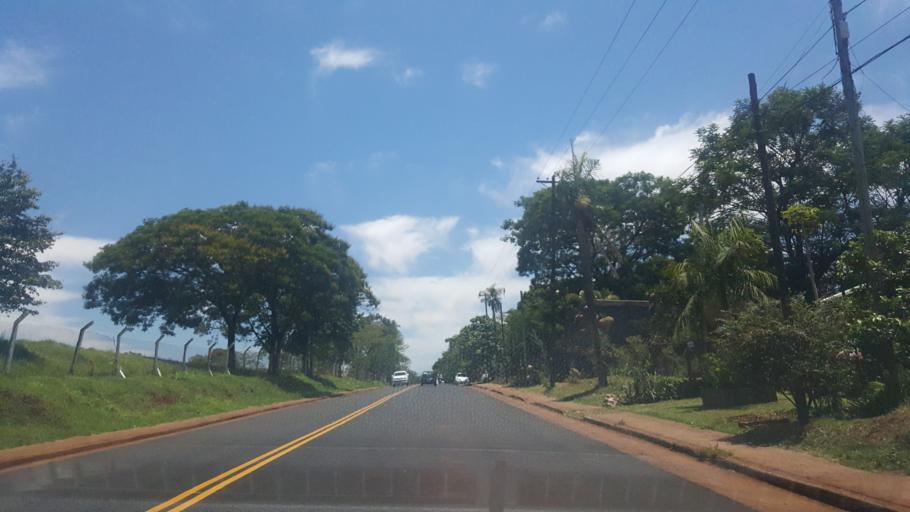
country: AR
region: Misiones
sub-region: Departamento de Capital
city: Posadas
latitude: -27.3617
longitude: -55.9206
